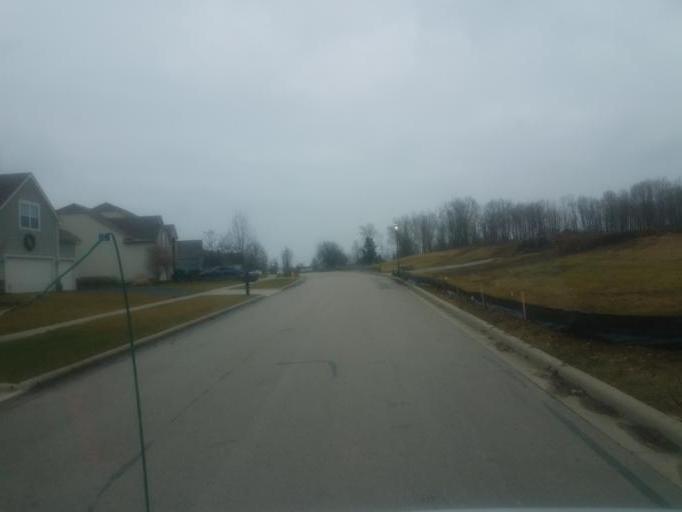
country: US
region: Ohio
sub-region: Delaware County
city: Sunbury
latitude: 40.2190
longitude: -82.8921
